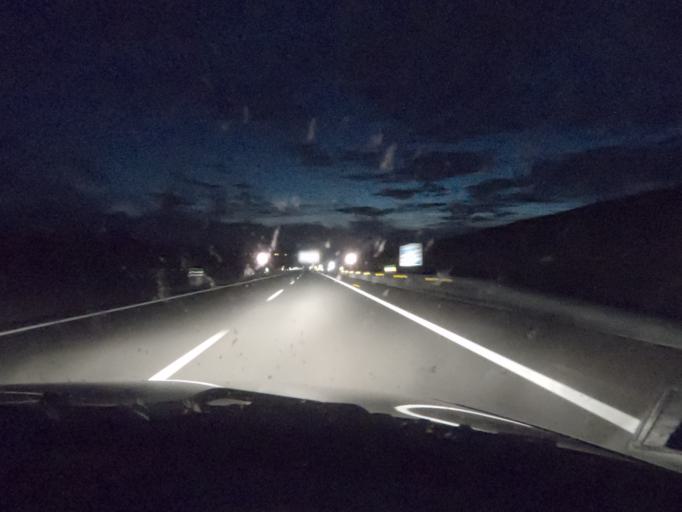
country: ES
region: Extremadura
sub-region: Provincia de Caceres
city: Coria
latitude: 40.0111
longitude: -6.5543
